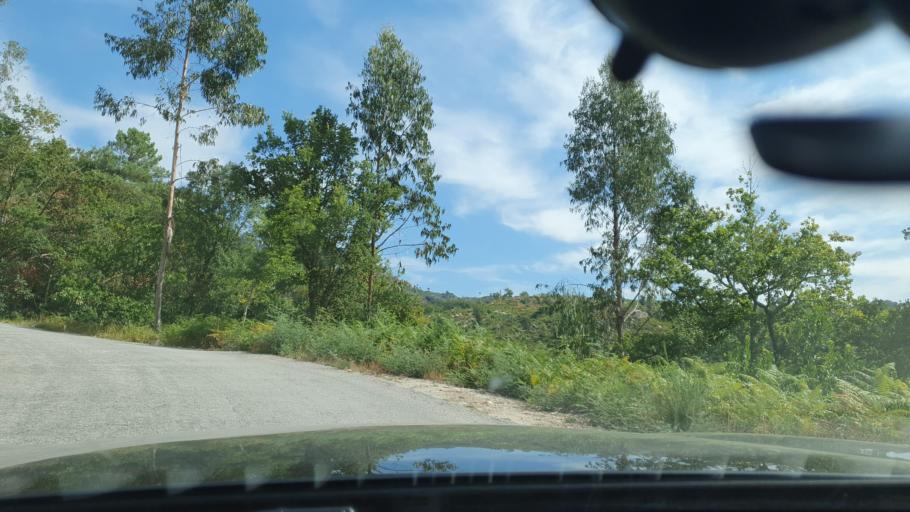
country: PT
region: Braga
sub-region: Vieira do Minho
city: Vieira do Minho
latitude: 41.6990
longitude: -8.0832
